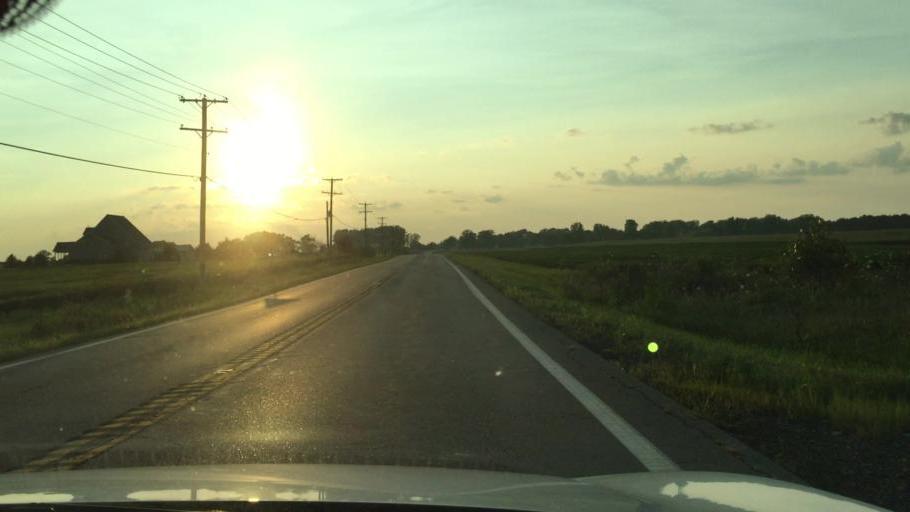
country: US
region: Ohio
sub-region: Madison County
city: Choctaw Lake
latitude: 39.9762
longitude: -83.3825
